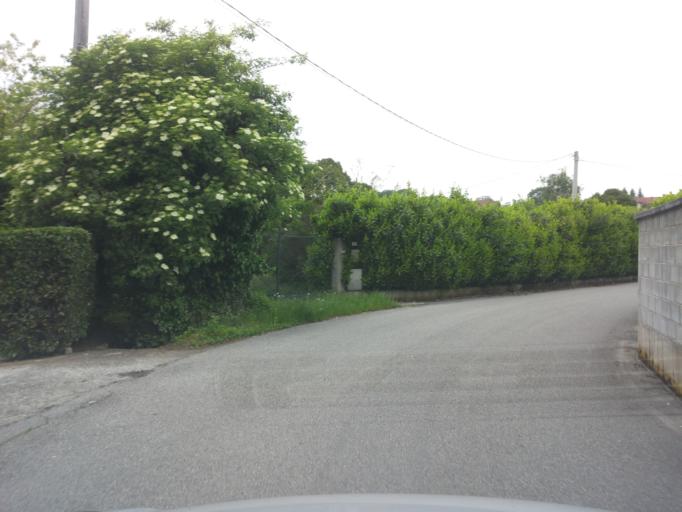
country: IT
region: Piedmont
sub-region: Provincia di Biella
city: Cavaglia
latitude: 45.4022
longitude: 8.0892
